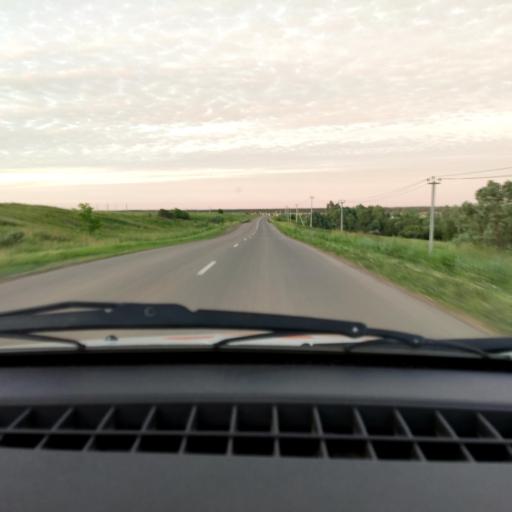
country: RU
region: Bashkortostan
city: Avdon
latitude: 54.5665
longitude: 55.7590
